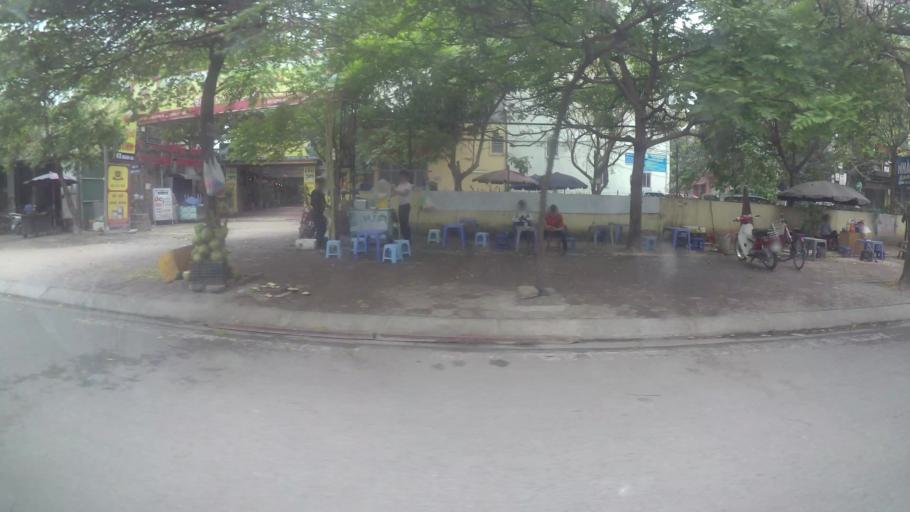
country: VN
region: Ha Noi
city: Tay Ho
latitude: 21.0690
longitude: 105.8026
